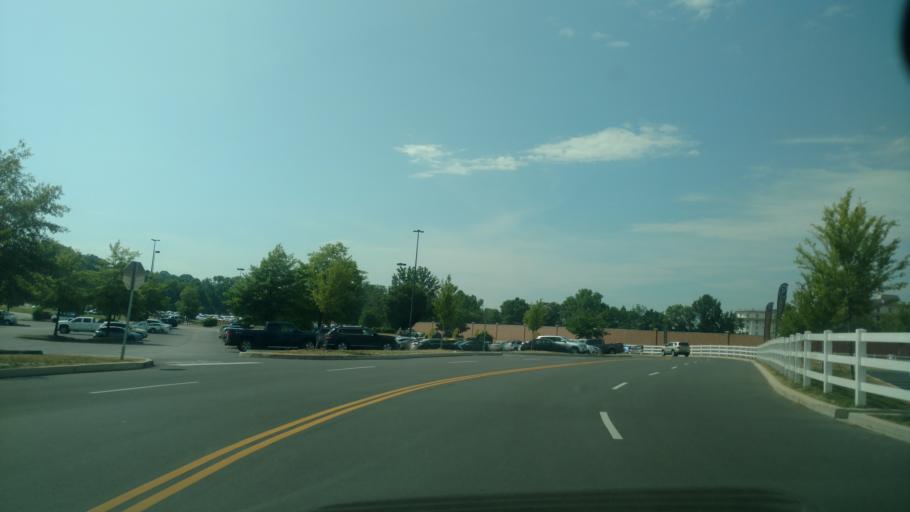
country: US
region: Tennessee
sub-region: Davidson County
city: Lakewood
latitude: 36.2079
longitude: -86.6954
